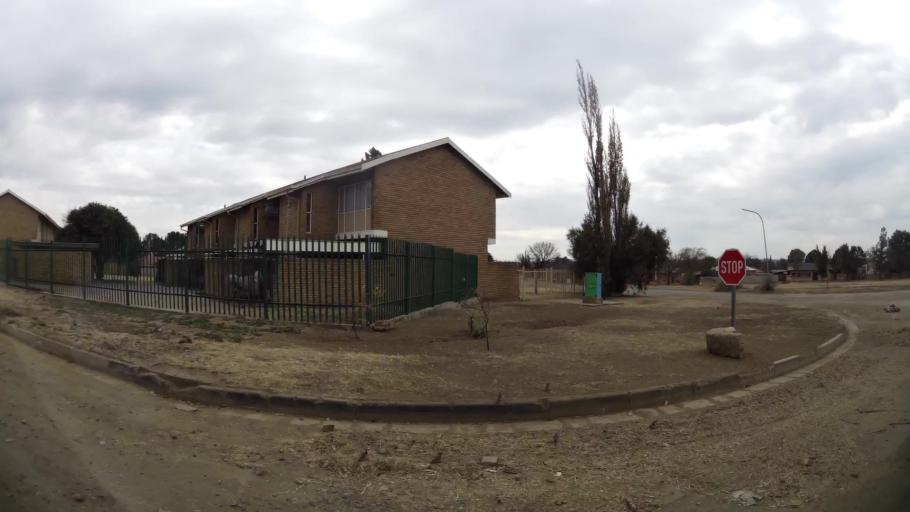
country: ZA
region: Orange Free State
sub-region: Fezile Dabi District Municipality
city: Kroonstad
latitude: -27.6795
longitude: 27.2338
